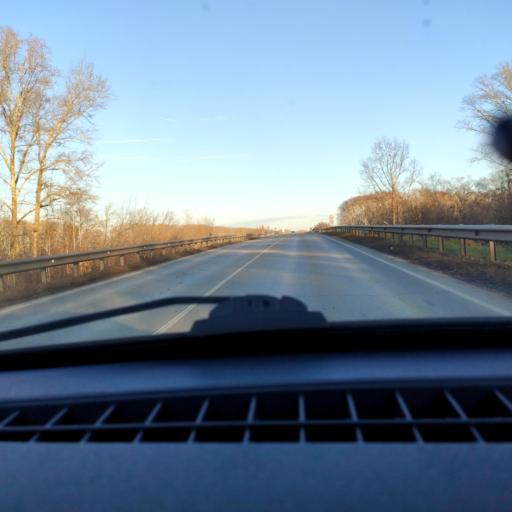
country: RU
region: Bashkortostan
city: Ufa
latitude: 54.6102
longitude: 55.8764
